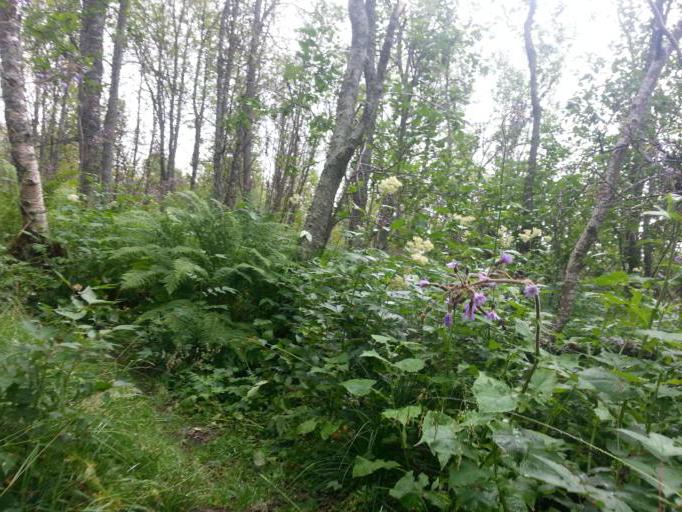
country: NO
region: Troms
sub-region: Tromso
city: Tromso
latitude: 69.6358
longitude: 18.9063
